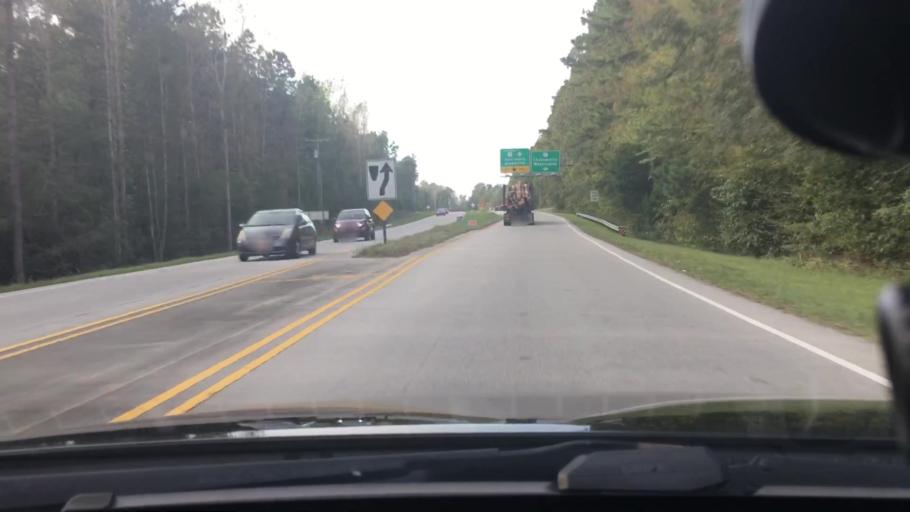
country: US
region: North Carolina
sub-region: Craven County
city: Vanceboro
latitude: 35.2831
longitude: -77.1248
